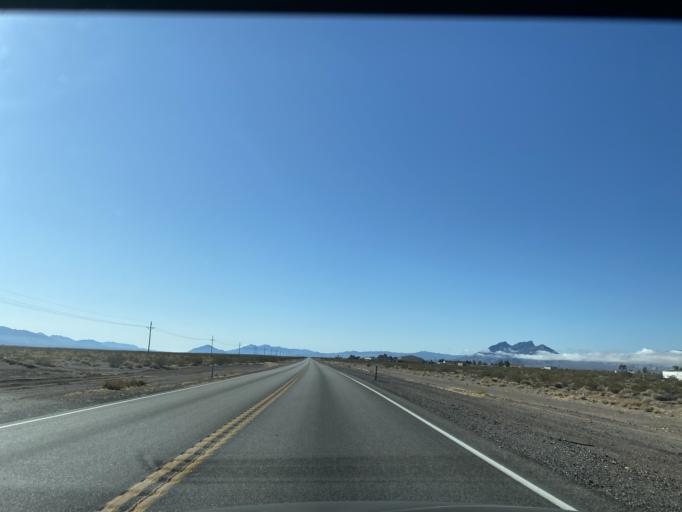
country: US
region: Nevada
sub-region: Nye County
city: Beatty
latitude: 36.5037
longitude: -116.4213
